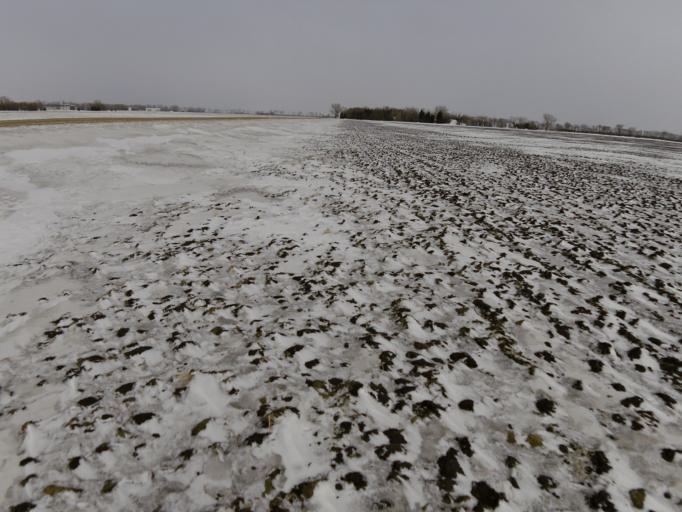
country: US
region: North Dakota
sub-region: Walsh County
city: Grafton
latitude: 48.3999
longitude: -97.2118
